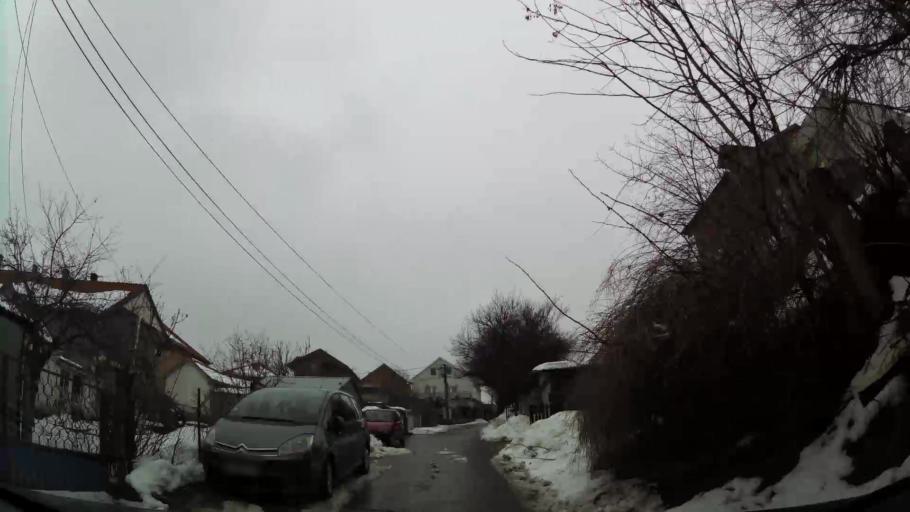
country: RS
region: Central Serbia
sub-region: Belgrade
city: Zvezdara
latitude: 44.7568
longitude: 20.5172
